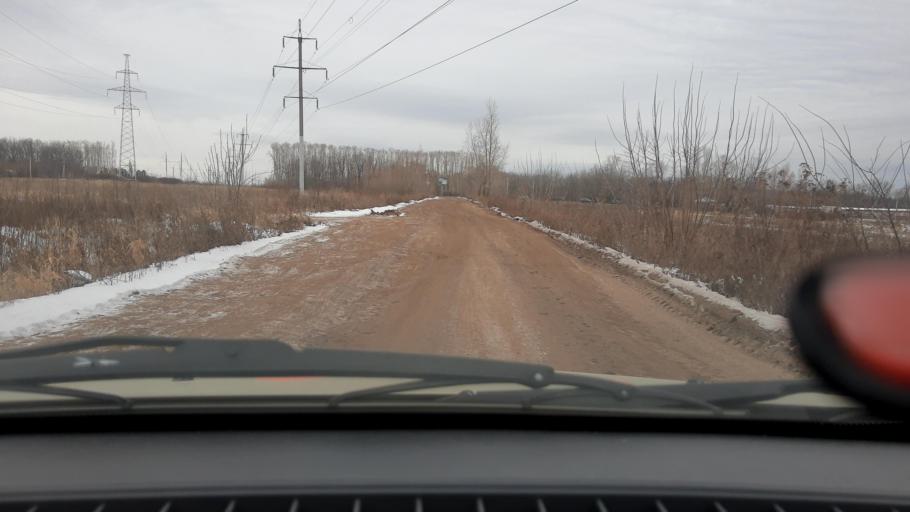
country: RU
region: Bashkortostan
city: Kabakovo
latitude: 54.6355
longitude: 56.0984
